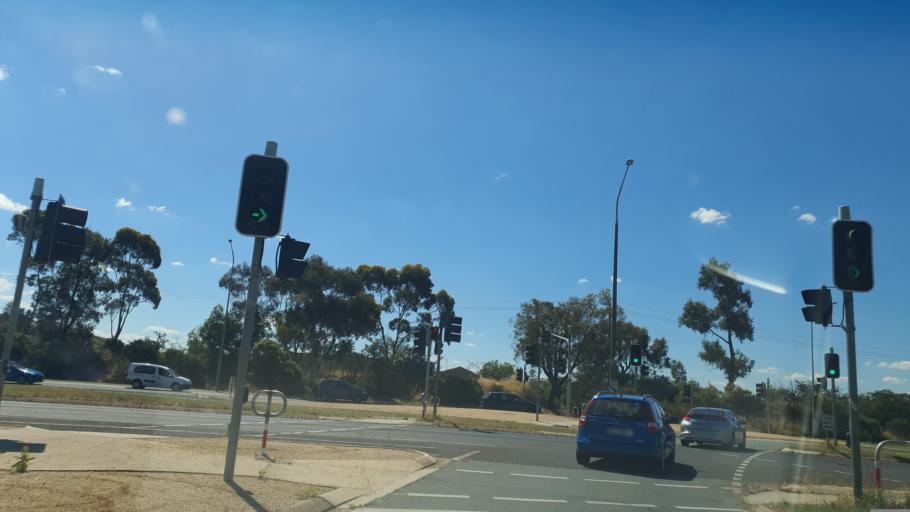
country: AU
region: Australian Capital Territory
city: Macquarie
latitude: -35.2281
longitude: 149.0601
